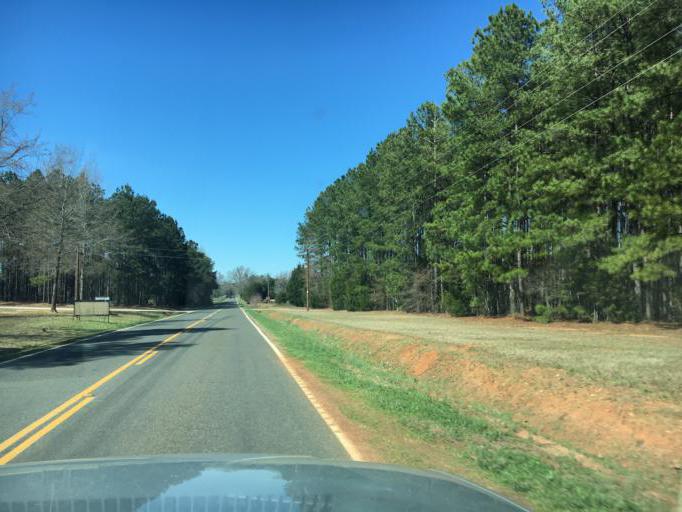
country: US
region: South Carolina
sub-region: Greenwood County
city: Ninety Six
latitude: 34.2787
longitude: -81.9487
